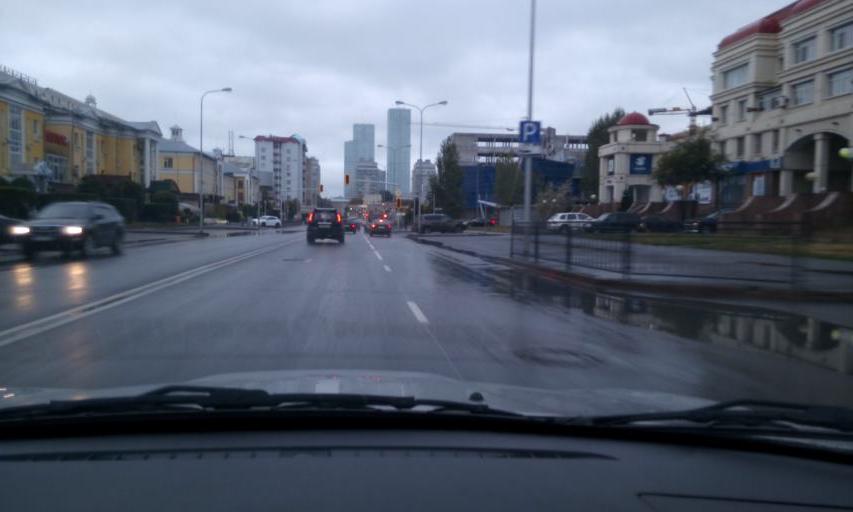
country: KZ
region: Astana Qalasy
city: Astana
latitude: 51.1635
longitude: 71.4338
